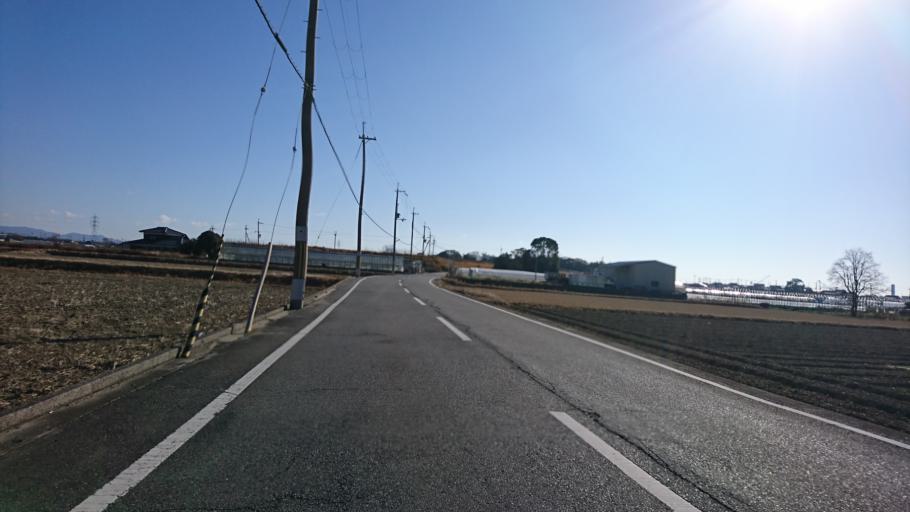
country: JP
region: Hyogo
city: Miki
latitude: 34.7270
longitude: 134.9553
